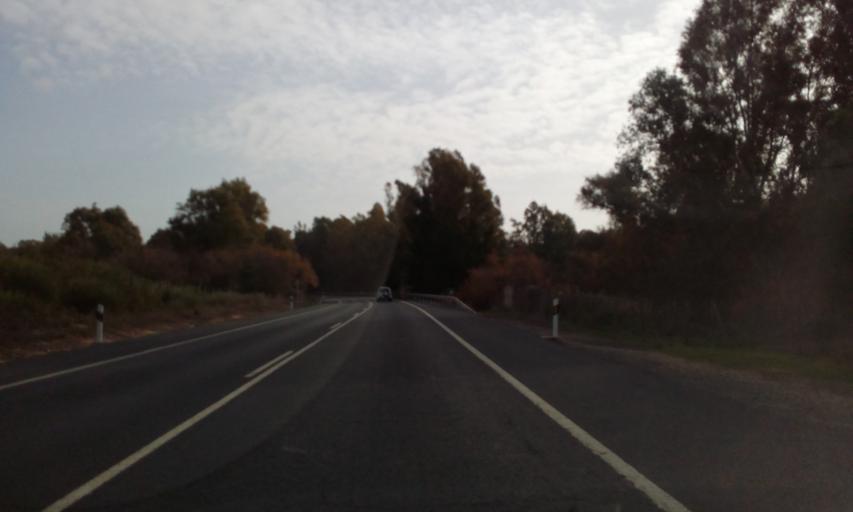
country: ES
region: Andalusia
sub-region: Provincia de Huelva
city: Palos de la Frontera
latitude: 37.1648
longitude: -6.8896
